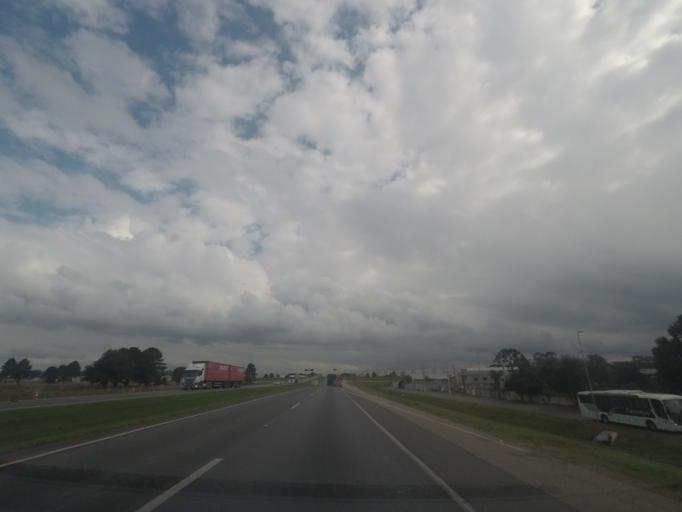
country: BR
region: Parana
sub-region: Piraquara
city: Piraquara
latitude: -25.5070
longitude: -49.1248
